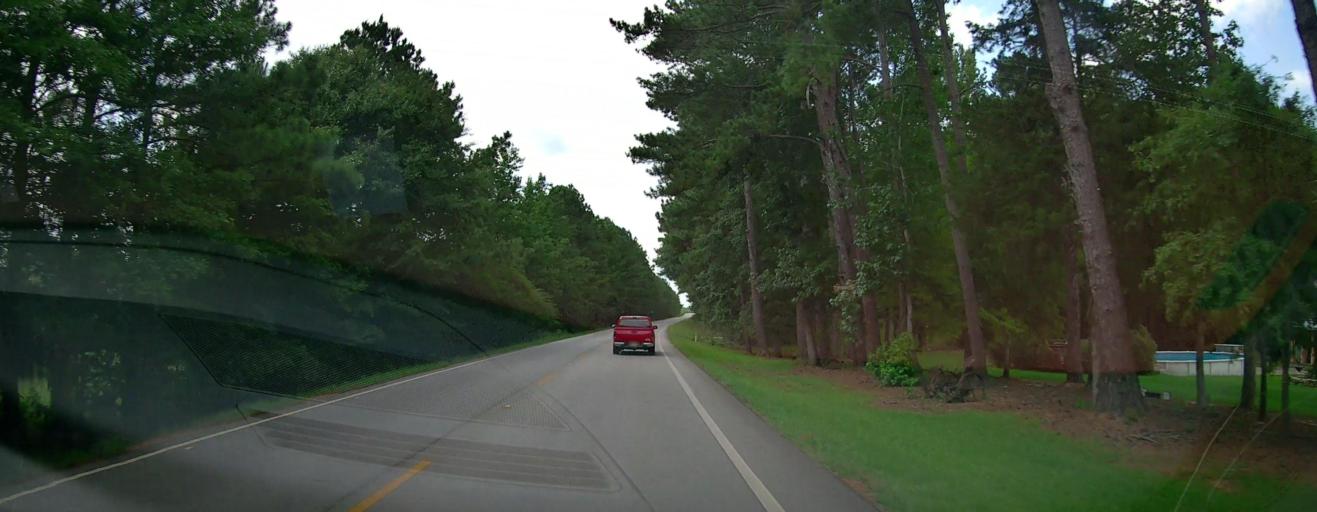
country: US
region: Georgia
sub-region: Meriwether County
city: Greenville
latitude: 33.0698
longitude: -84.7687
